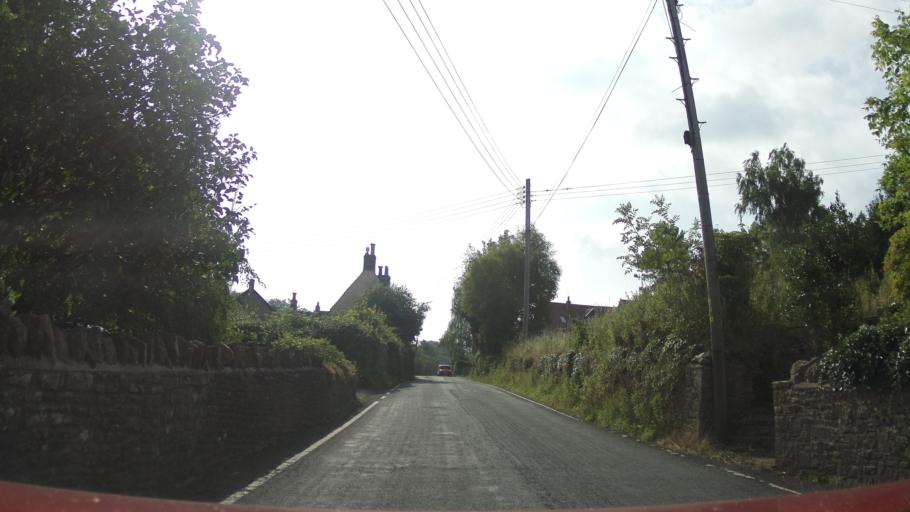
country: GB
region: England
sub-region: Bath and North East Somerset
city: Cameley
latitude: 51.2777
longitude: -2.5801
